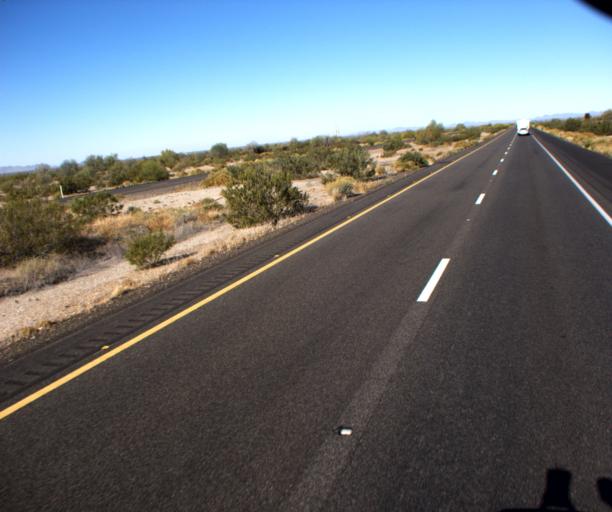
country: US
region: Arizona
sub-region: Maricopa County
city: Gila Bend
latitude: 32.9143
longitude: -112.6203
